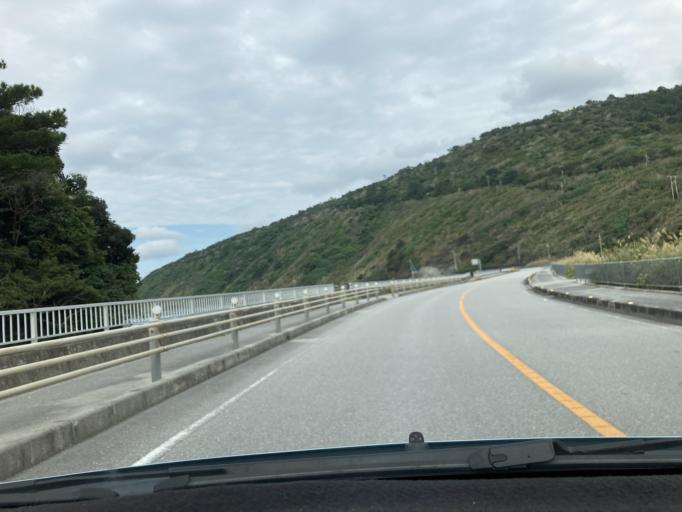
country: JP
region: Okinawa
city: Nago
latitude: 26.7873
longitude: 128.2210
